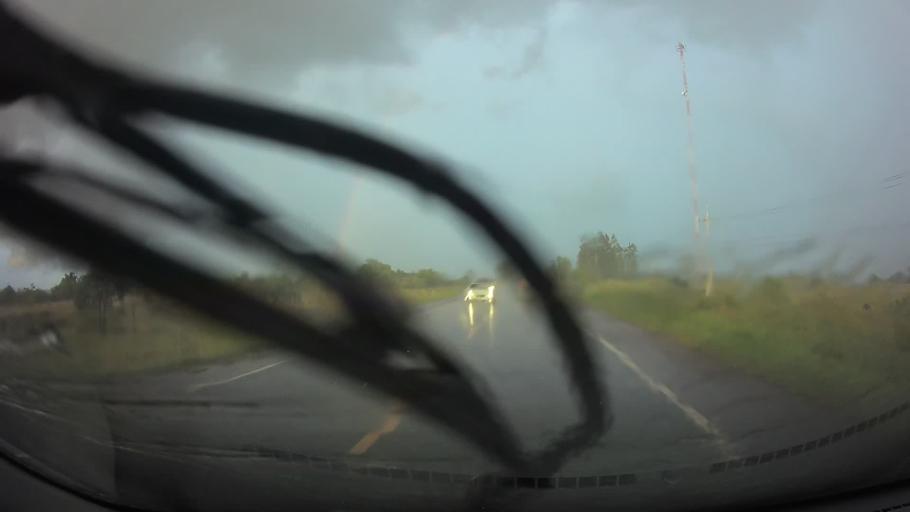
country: PY
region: Paraguari
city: Paraguari
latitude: -25.6980
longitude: -57.1752
